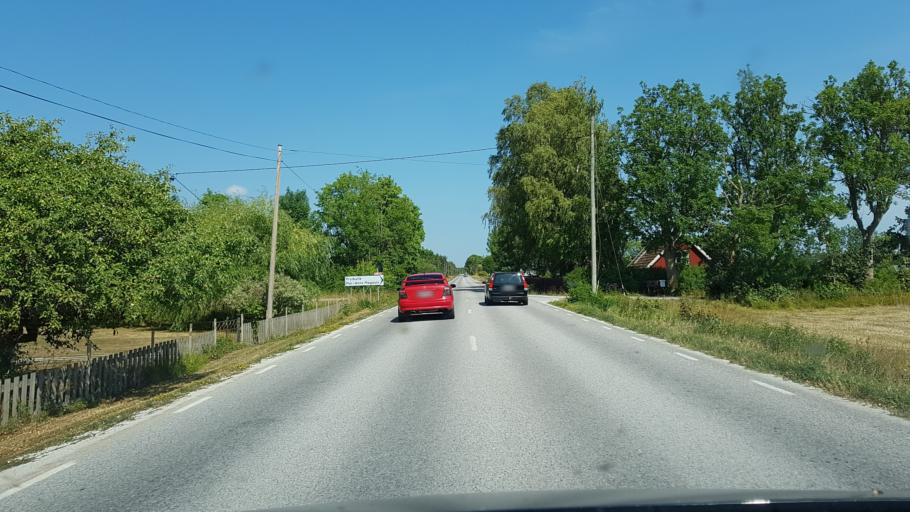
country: SE
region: Gotland
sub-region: Gotland
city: Visby
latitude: 57.6324
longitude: 18.4444
